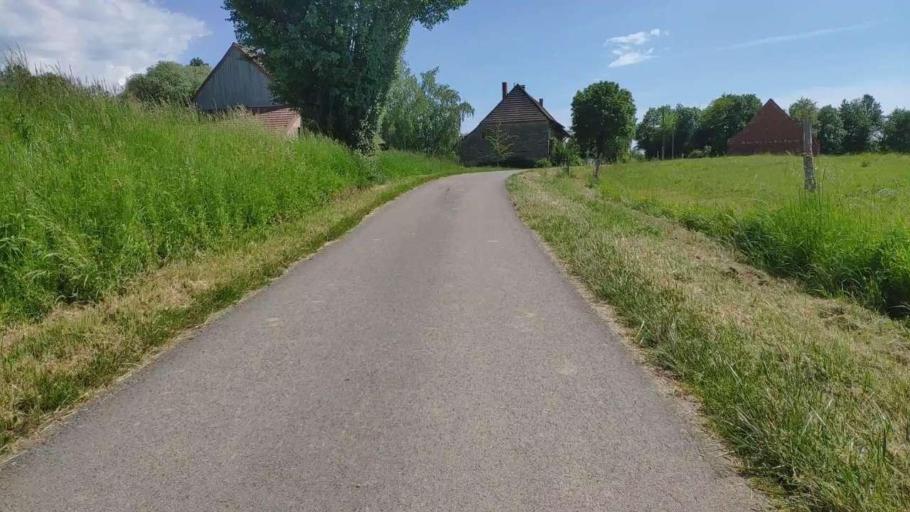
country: FR
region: Franche-Comte
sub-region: Departement du Jura
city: Bletterans
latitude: 46.7973
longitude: 5.4146
